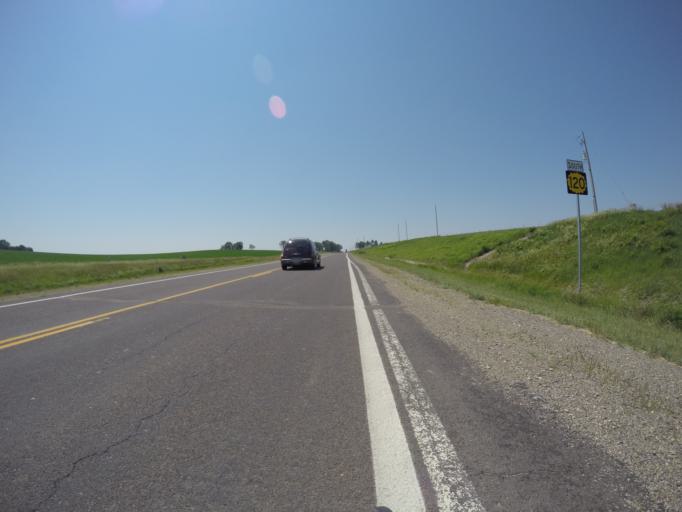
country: US
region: Kansas
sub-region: Doniphan County
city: Highland
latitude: 39.8388
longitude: -95.2652
